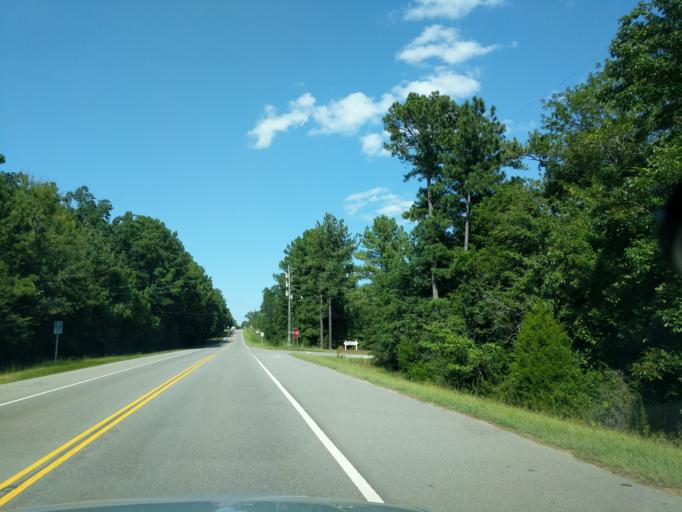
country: US
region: South Carolina
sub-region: Newberry County
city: Prosperity
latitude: 34.1038
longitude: -81.5674
